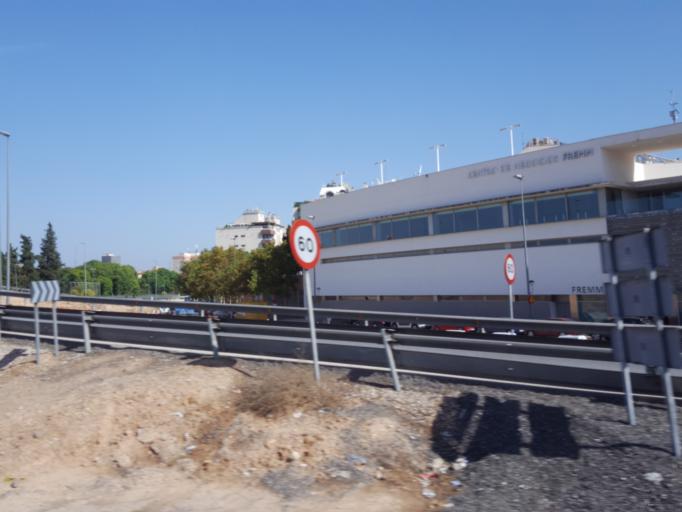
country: ES
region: Murcia
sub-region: Murcia
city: Murcia
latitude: 37.9900
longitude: -1.1448
